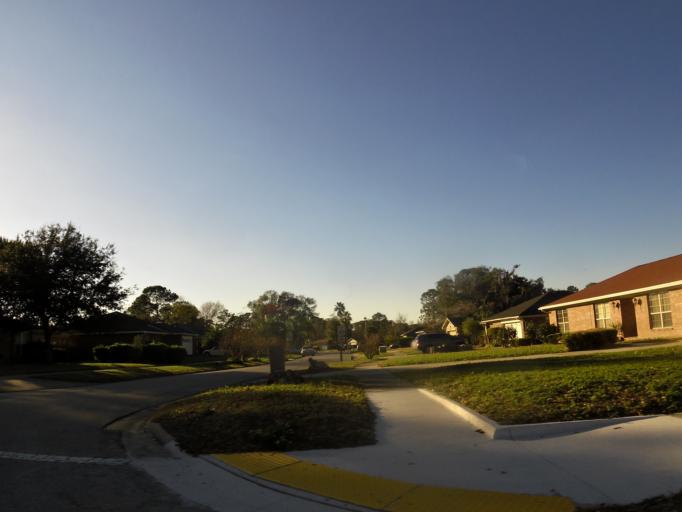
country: US
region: Florida
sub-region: Saint Johns County
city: Fruit Cove
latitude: 30.2188
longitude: -81.6005
